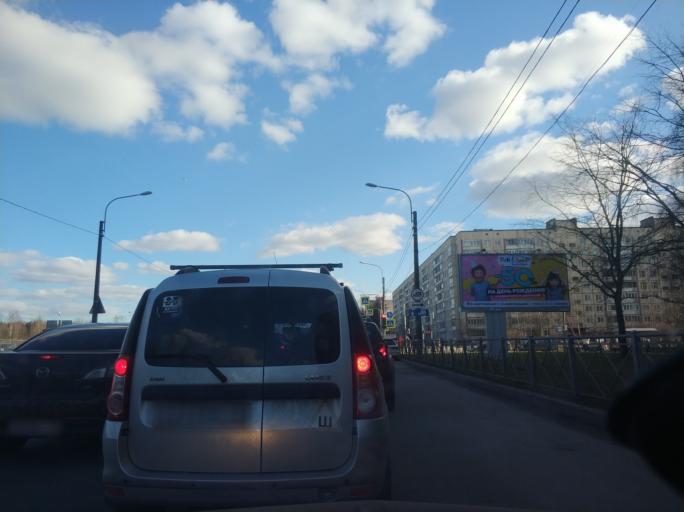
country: RU
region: St.-Petersburg
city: Krasnogvargeisky
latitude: 59.9540
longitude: 30.4966
